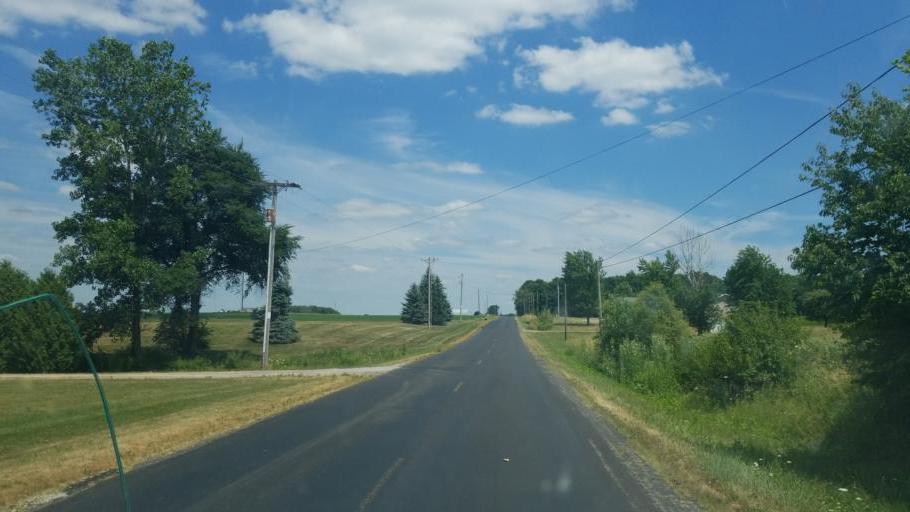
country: US
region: Ohio
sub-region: Williams County
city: Edgerton
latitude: 41.4662
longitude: -84.7061
